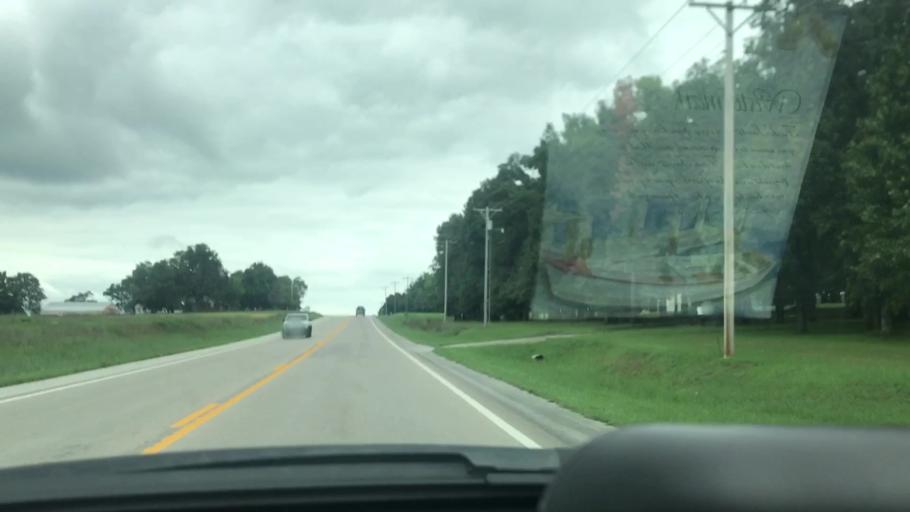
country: US
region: Missouri
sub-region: Dallas County
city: Buffalo
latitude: 37.6714
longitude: -93.1033
